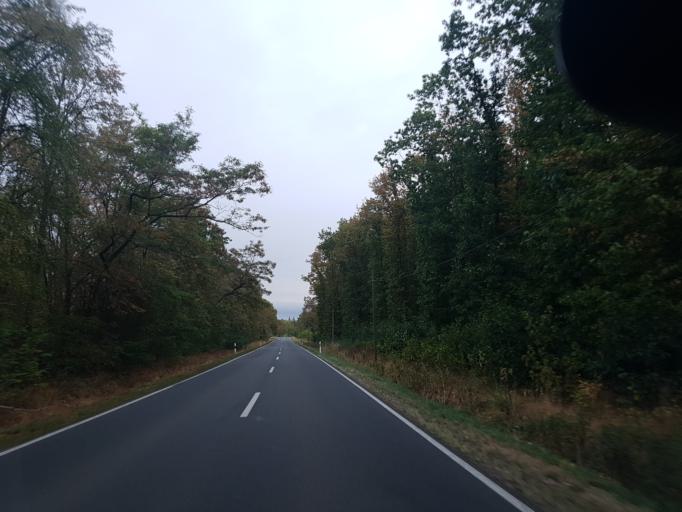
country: DE
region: Saxony
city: Beilrode
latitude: 51.6133
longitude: 13.0427
